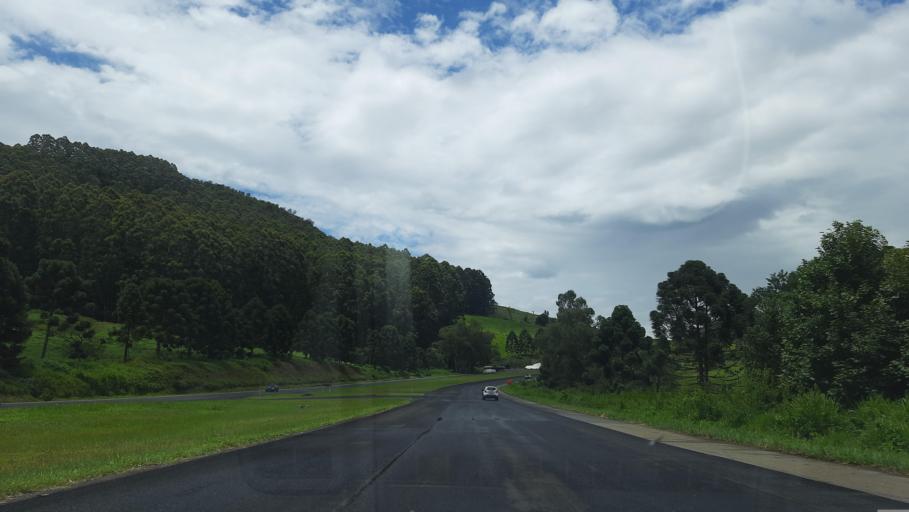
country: BR
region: Minas Gerais
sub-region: Pocos De Caldas
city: Pocos de Caldas
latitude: -21.8288
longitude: -46.6711
